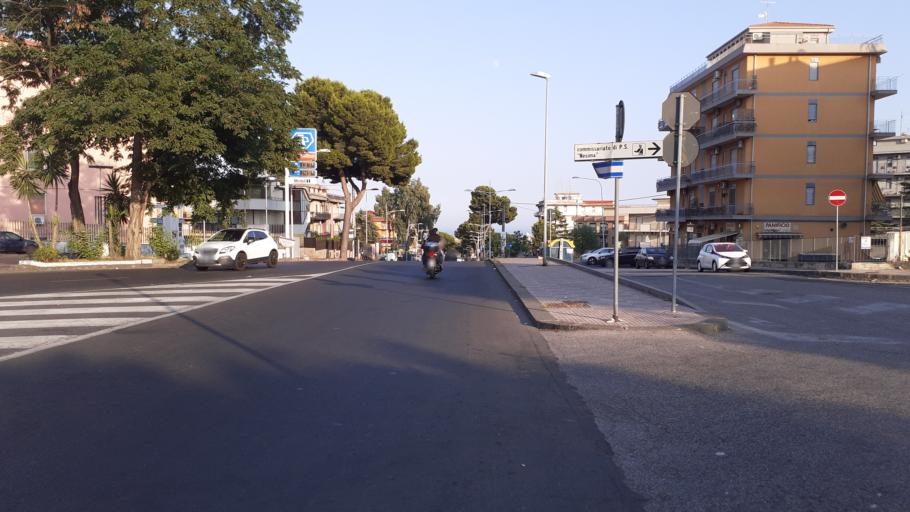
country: IT
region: Sicily
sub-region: Catania
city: Misterbianco
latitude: 37.5074
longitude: 15.0507
